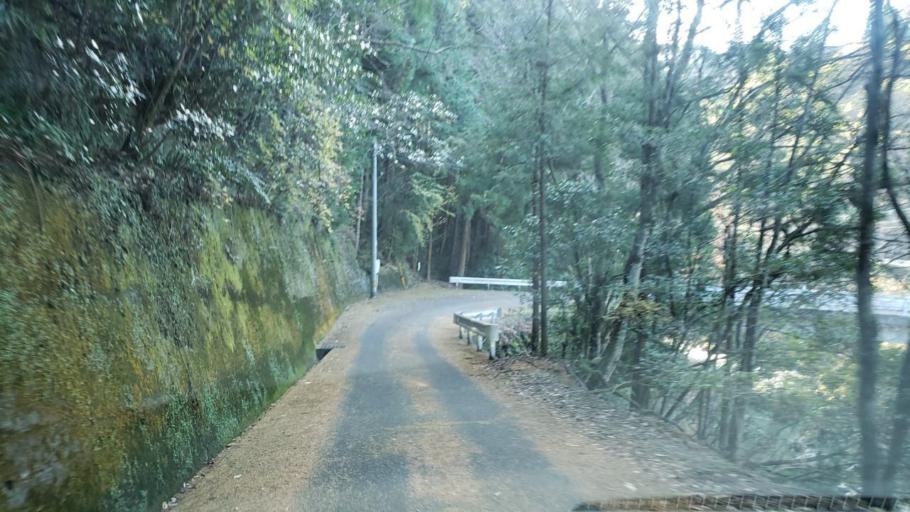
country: JP
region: Tokushima
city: Wakimachi
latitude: 34.0204
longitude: 134.0393
